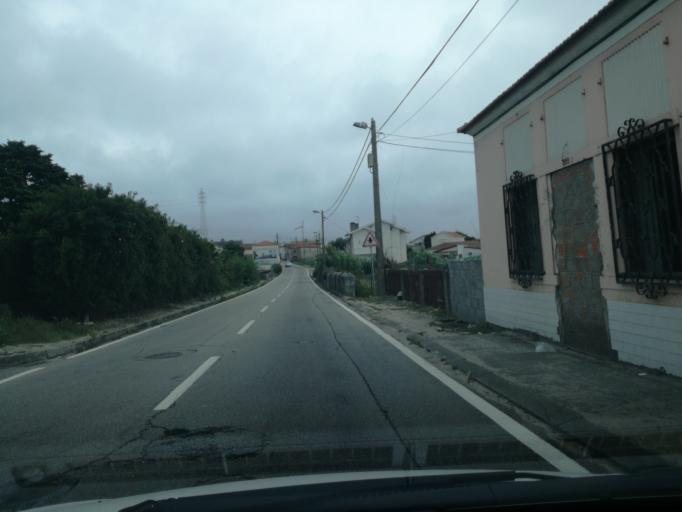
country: PT
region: Aveiro
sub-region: Espinho
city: Espinho
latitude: 40.9987
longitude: -8.6365
